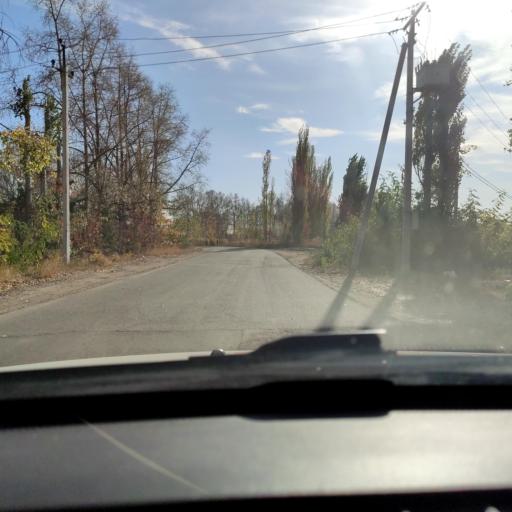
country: RU
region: Voronezj
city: Podgornoye
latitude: 51.8042
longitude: 39.1991
